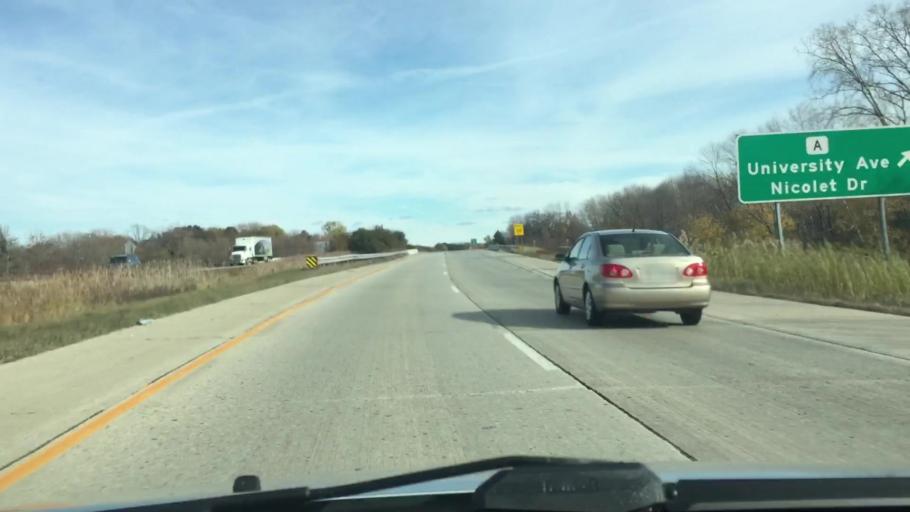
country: US
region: Wisconsin
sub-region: Brown County
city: Green Bay
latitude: 44.5252
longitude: -87.9425
